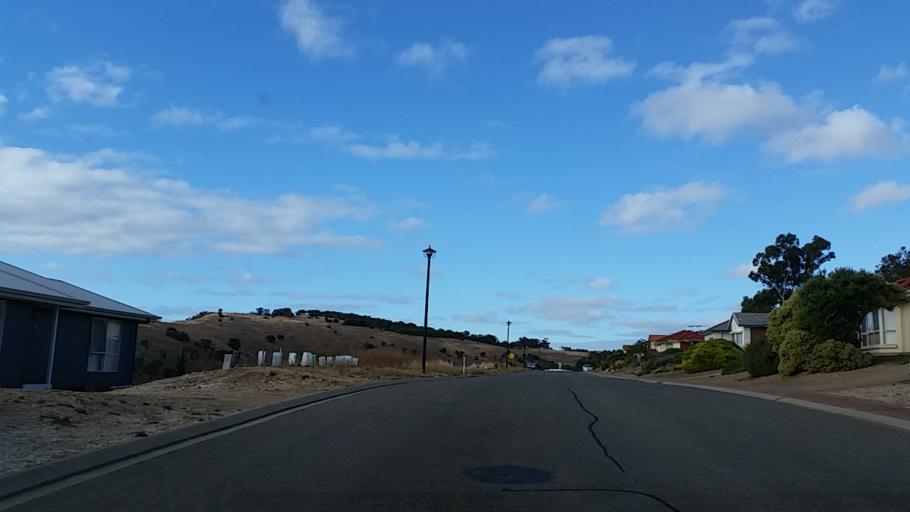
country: AU
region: South Australia
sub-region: Yankalilla
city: Normanville
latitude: -35.5037
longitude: 138.2480
